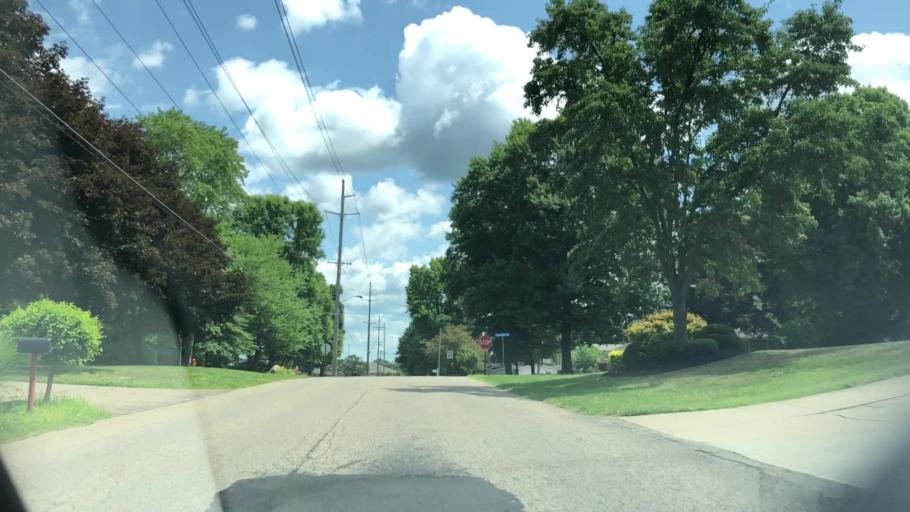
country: US
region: Ohio
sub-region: Stark County
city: Massillon
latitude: 40.8211
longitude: -81.5071
